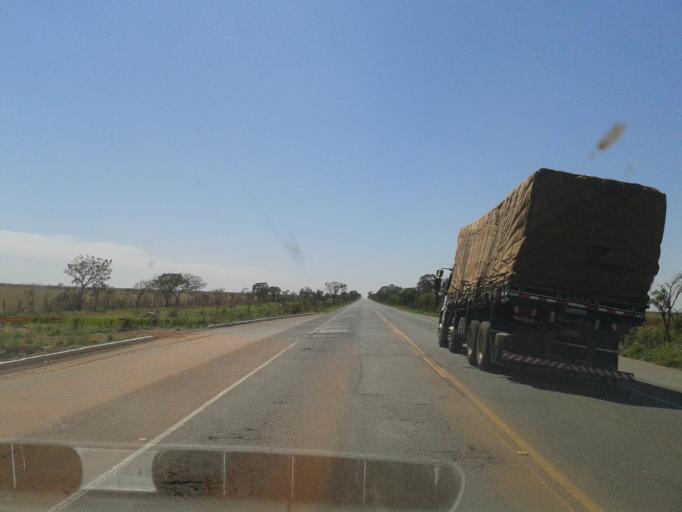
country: BR
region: Minas Gerais
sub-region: Monte Carmelo
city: Monte Carmelo
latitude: -19.2943
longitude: -47.4814
